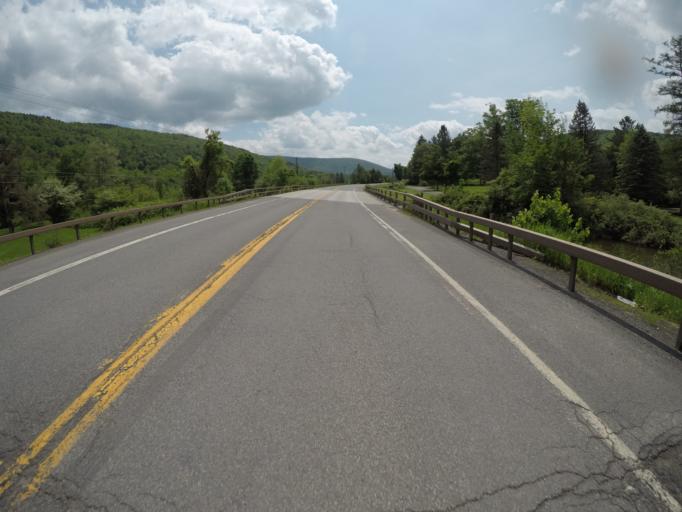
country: US
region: New York
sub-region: Delaware County
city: Stamford
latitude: 42.1704
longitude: -74.6113
